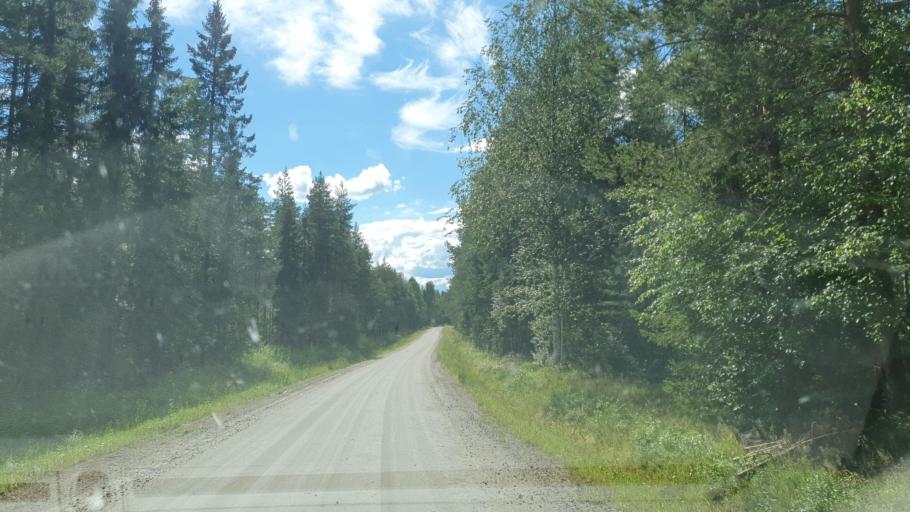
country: FI
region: Kainuu
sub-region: Kehys-Kainuu
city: Kuhmo
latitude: 64.1633
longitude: 29.8534
